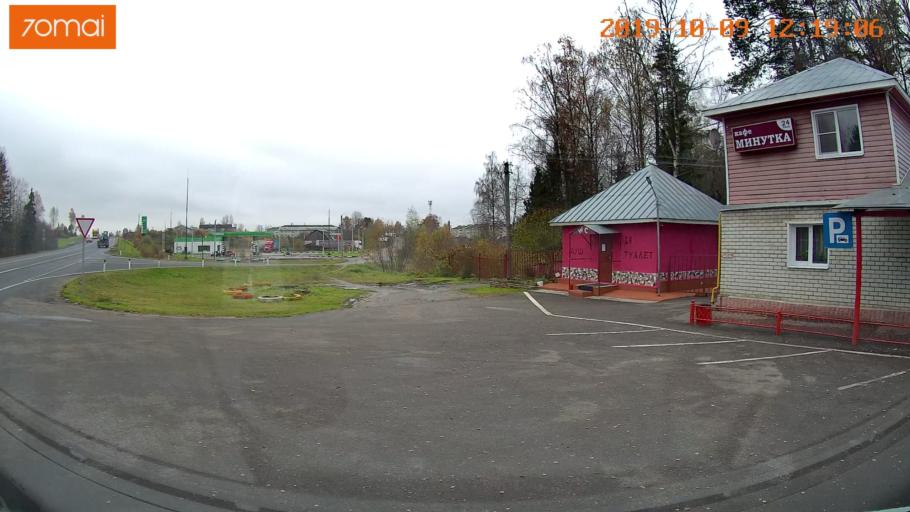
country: RU
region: Jaroslavl
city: Prechistoye
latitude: 58.4360
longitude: 40.3215
